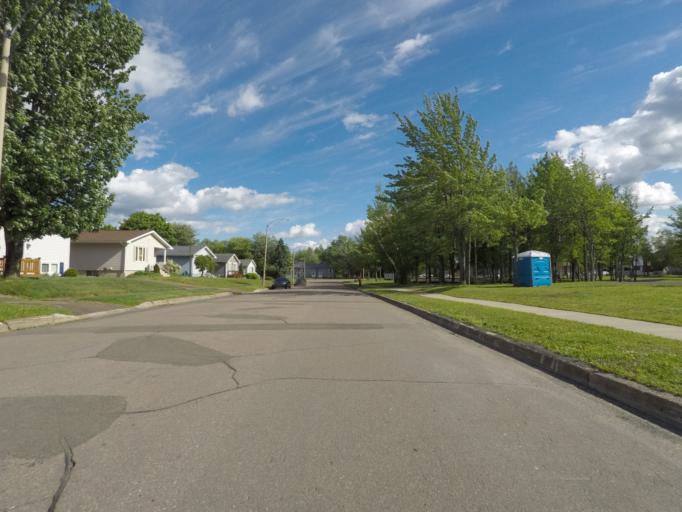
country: CA
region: New Brunswick
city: Moncton
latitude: 46.1002
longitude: -64.8243
